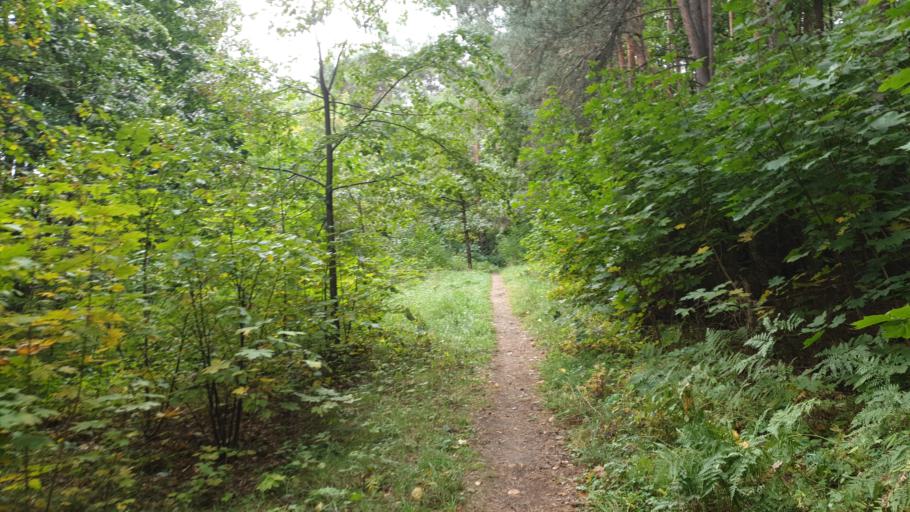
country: LT
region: Vilnius County
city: Seskine
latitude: 54.6991
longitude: 25.2358
